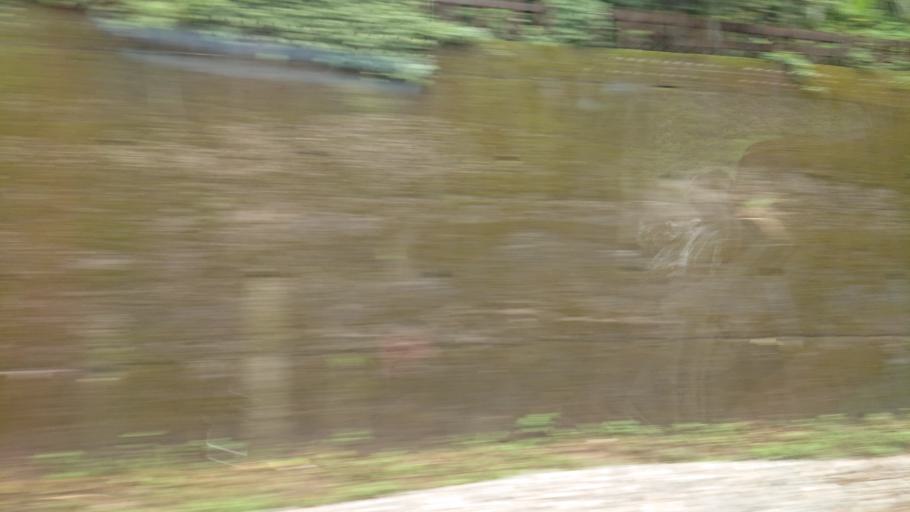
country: TW
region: Taiwan
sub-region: Keelung
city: Keelung
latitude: 25.0966
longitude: 121.8324
